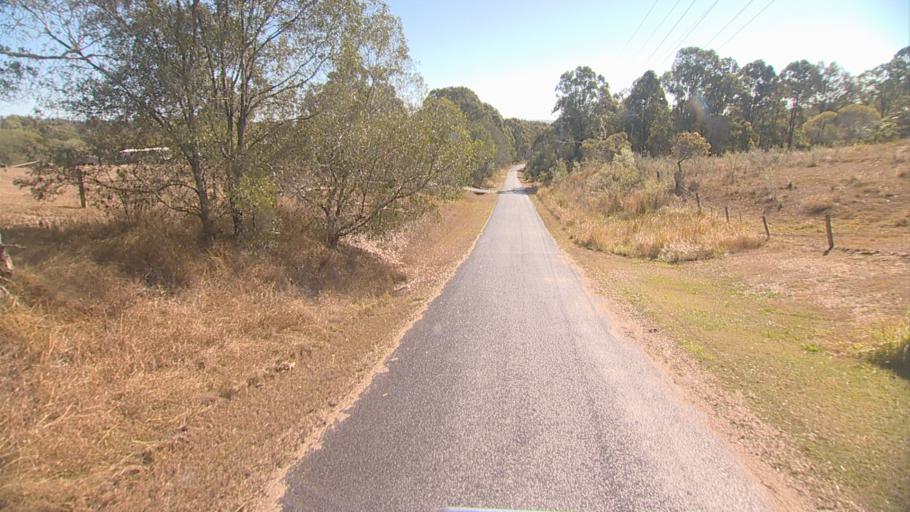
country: AU
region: Queensland
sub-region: Logan
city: Cedar Vale
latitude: -27.9004
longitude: 153.0221
